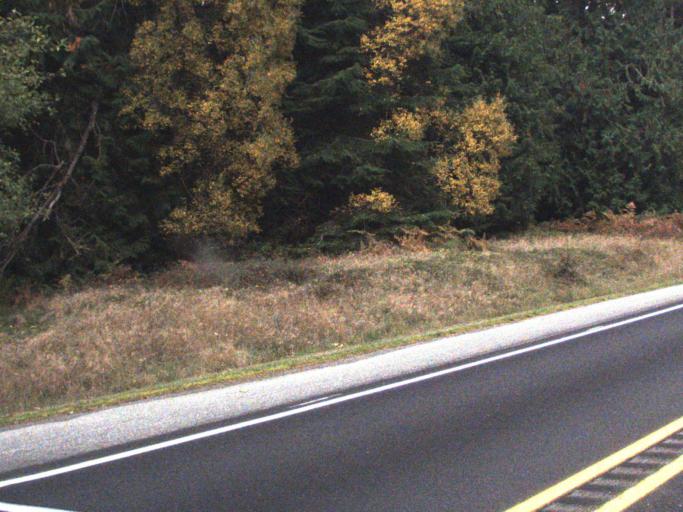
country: US
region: Washington
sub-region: Island County
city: Freeland
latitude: 48.0785
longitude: -122.5700
